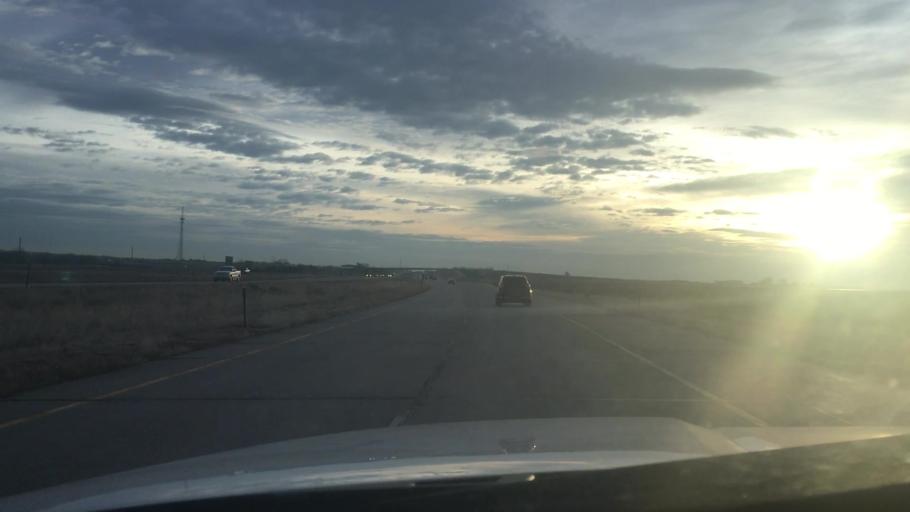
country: US
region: Colorado
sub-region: Morgan County
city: Fort Morgan
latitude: 40.2423
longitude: -103.9387
